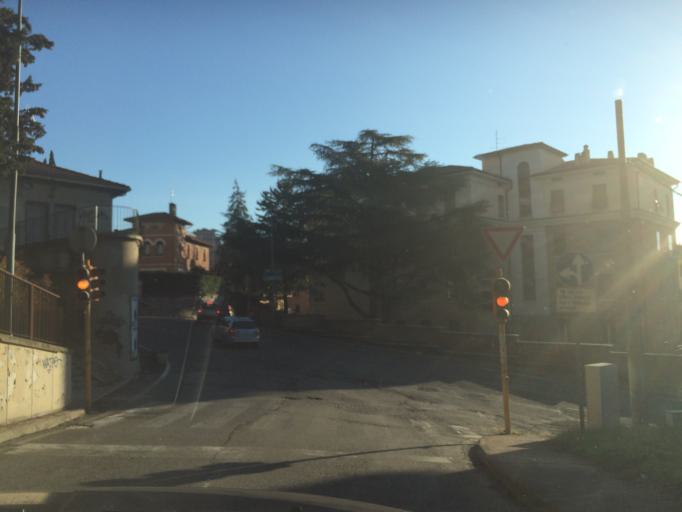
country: IT
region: Umbria
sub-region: Provincia di Perugia
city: Perugia
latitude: 43.1028
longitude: 12.3869
